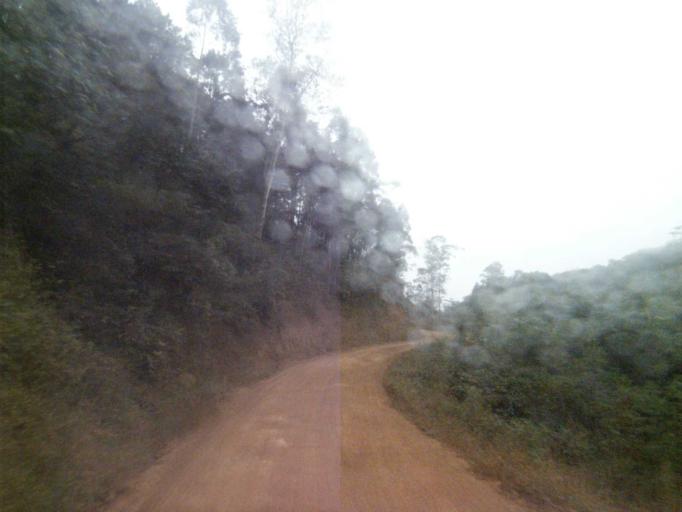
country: BR
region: Santa Catarina
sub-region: Anitapolis
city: Anitapolis
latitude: -27.8907
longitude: -49.1316
